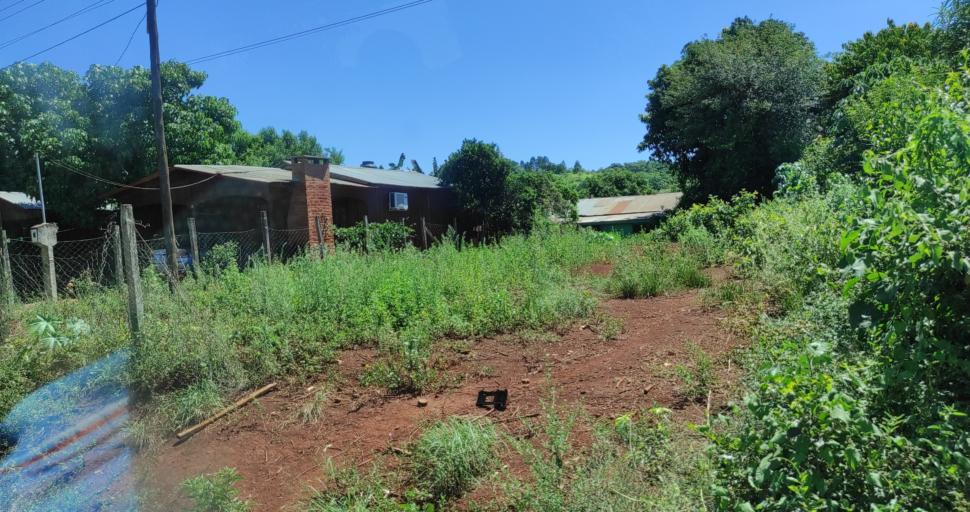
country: AR
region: Misiones
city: El Soberbio
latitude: -27.3026
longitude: -54.1938
